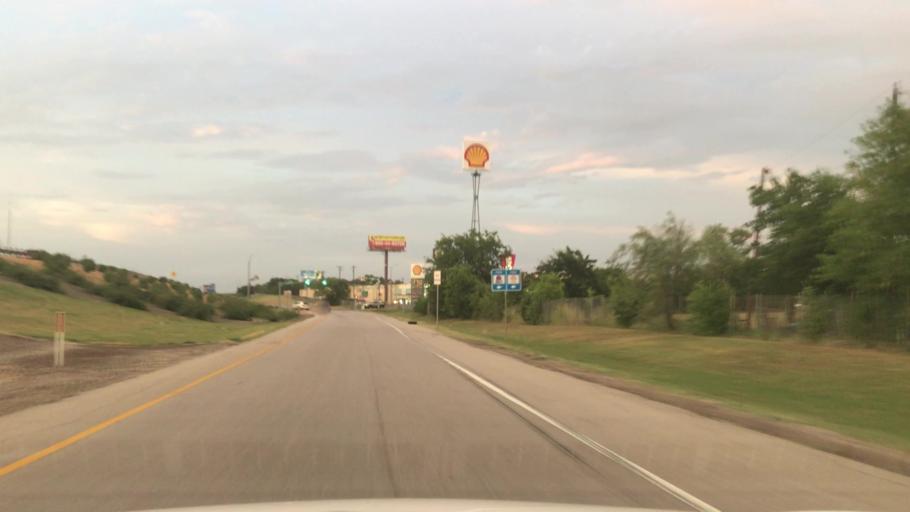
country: US
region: Texas
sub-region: Dallas County
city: Balch Springs
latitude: 32.7180
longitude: -96.6163
